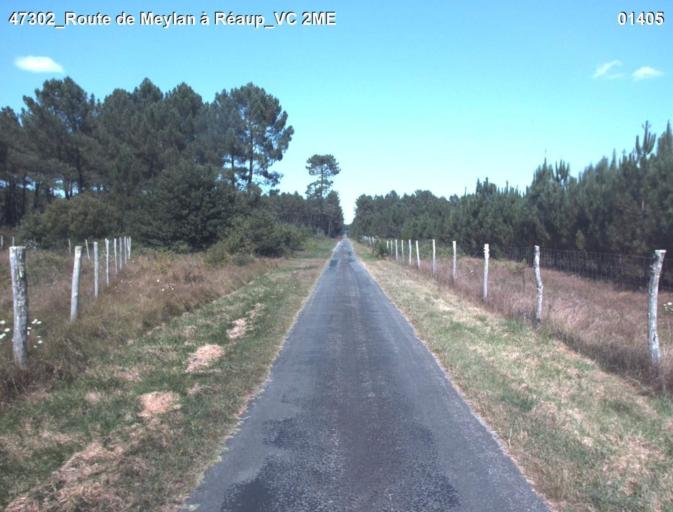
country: FR
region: Aquitaine
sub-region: Departement du Lot-et-Garonne
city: Mezin
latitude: 44.0965
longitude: 0.1327
